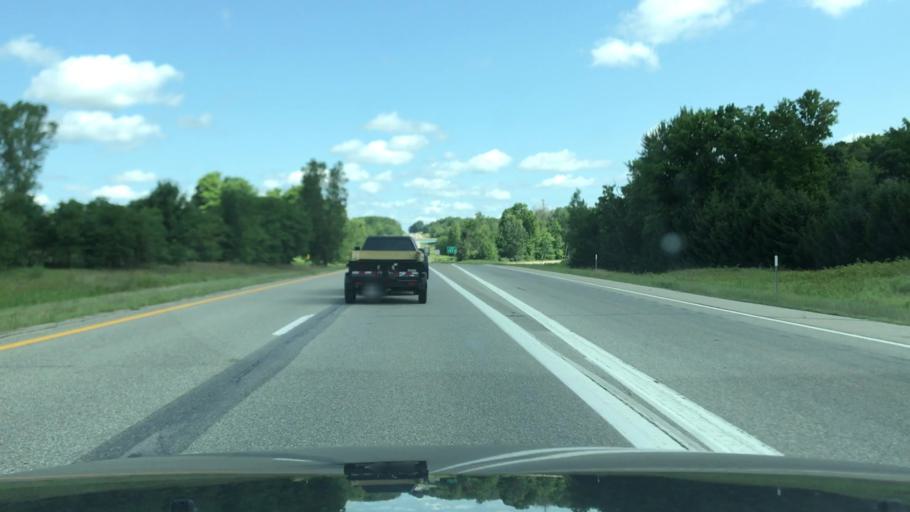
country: US
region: Michigan
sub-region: Mecosta County
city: Big Rapids
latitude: 43.7366
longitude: -85.5320
